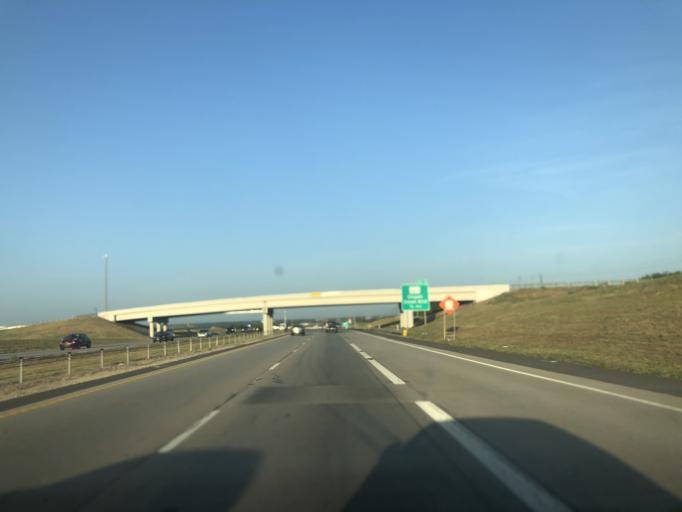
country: US
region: Texas
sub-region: Tarrant County
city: White Settlement
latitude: 32.7341
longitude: -97.4939
